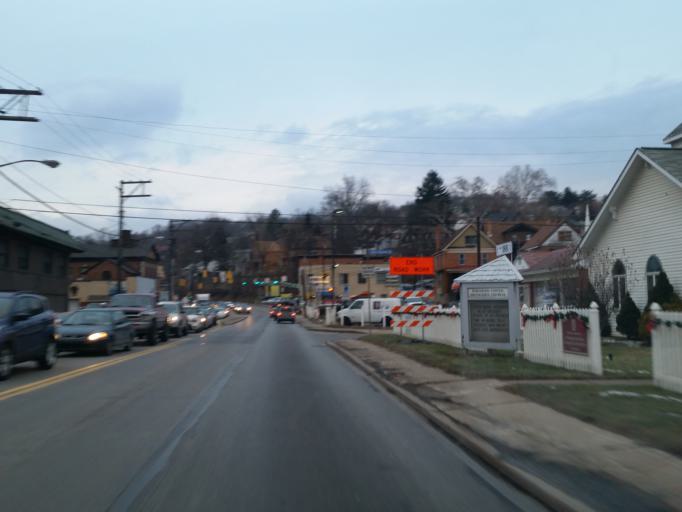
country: US
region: Pennsylvania
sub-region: Allegheny County
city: Whitehall
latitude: 40.3838
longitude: -79.9956
